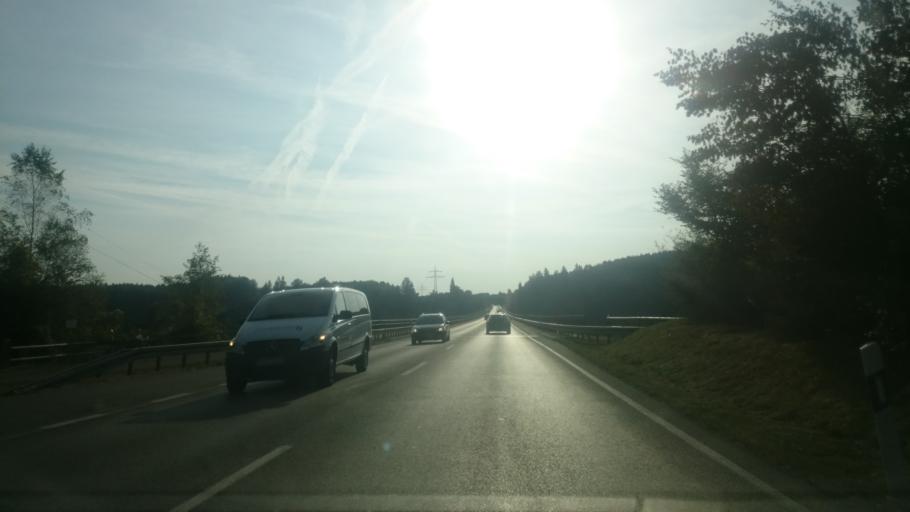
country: DE
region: Bavaria
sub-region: Upper Bavaria
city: Schongau
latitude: 47.7890
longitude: 10.8849
